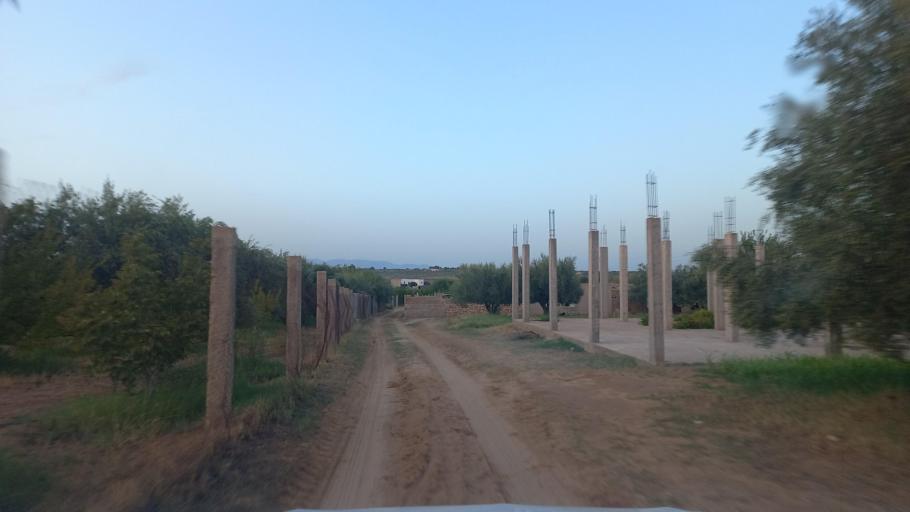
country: TN
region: Al Qasrayn
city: Kasserine
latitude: 35.2170
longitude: 9.0525
